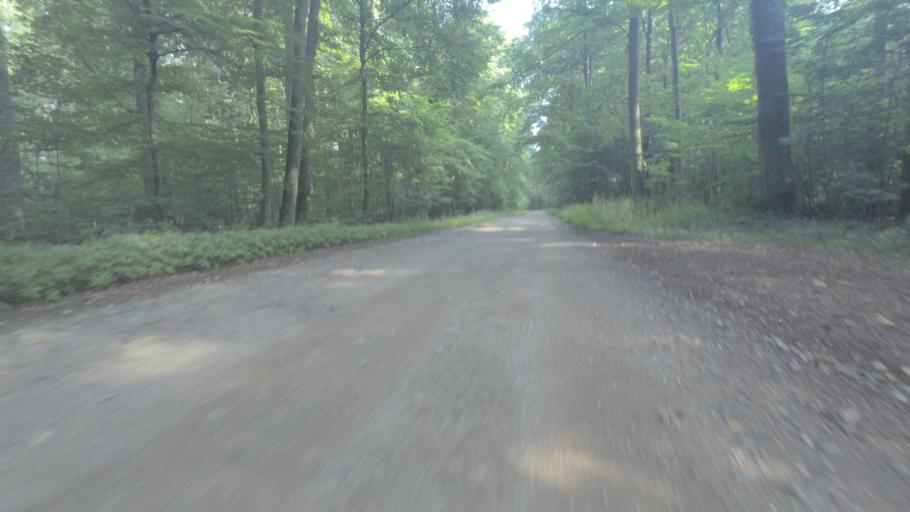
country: DE
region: Brandenburg
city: Wittstock
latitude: 53.2528
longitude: 12.4709
